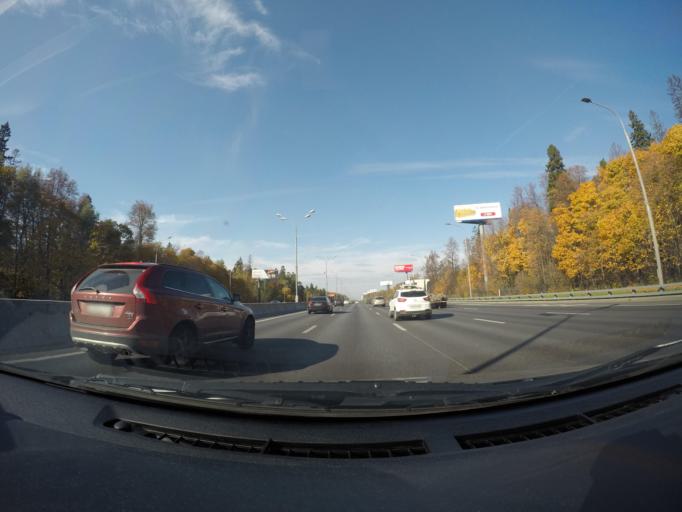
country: RU
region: Moscow
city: Gol'yanovo
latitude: 55.8500
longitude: 37.7893
